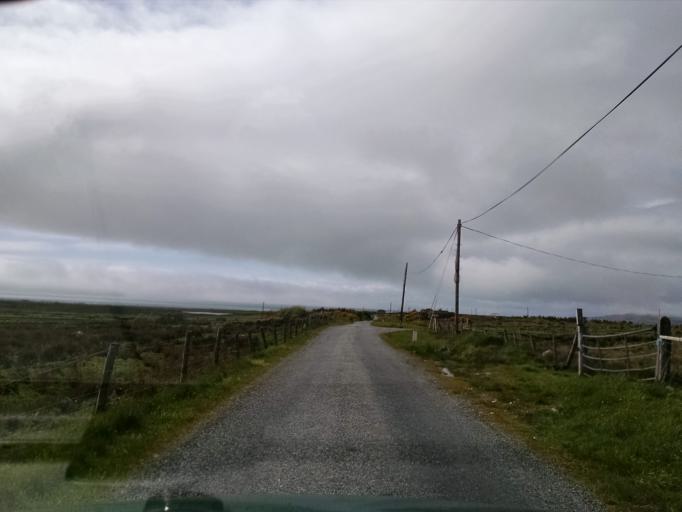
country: IE
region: Connaught
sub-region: County Galway
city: Clifden
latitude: 53.7397
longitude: -9.8608
